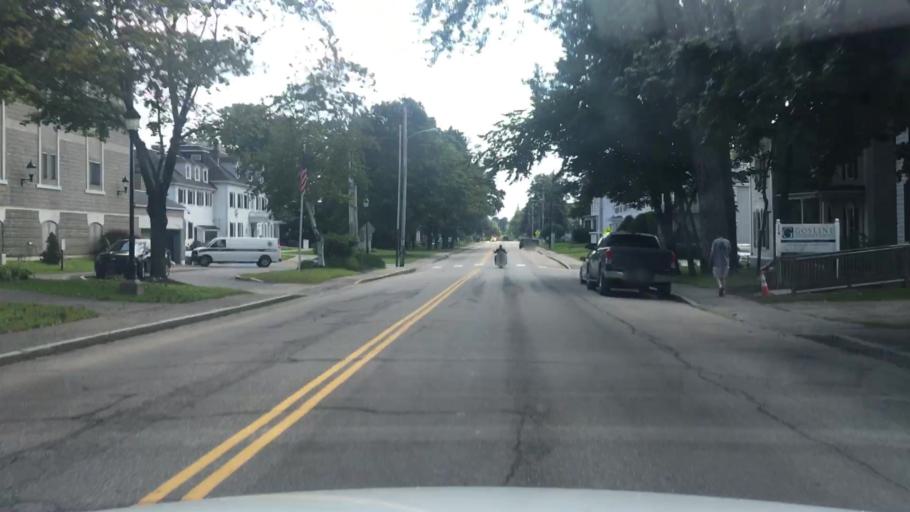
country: US
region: Maine
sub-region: Kennebec County
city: Augusta
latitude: 44.3144
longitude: -69.7779
